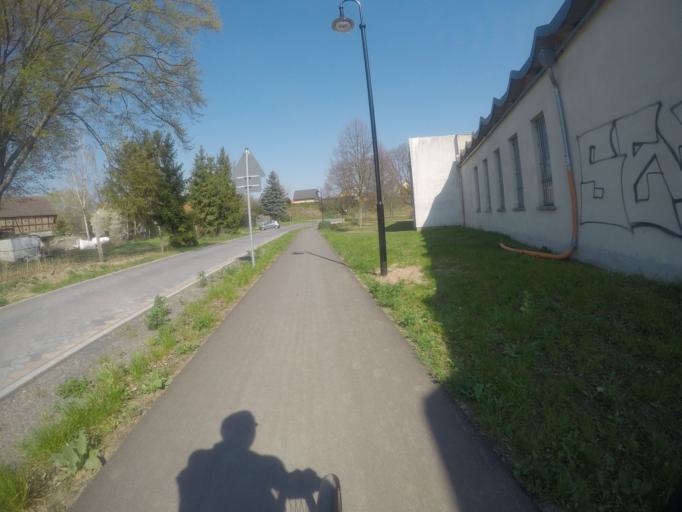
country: DE
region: Brandenburg
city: Brieselang
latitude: 52.6522
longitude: 13.0102
